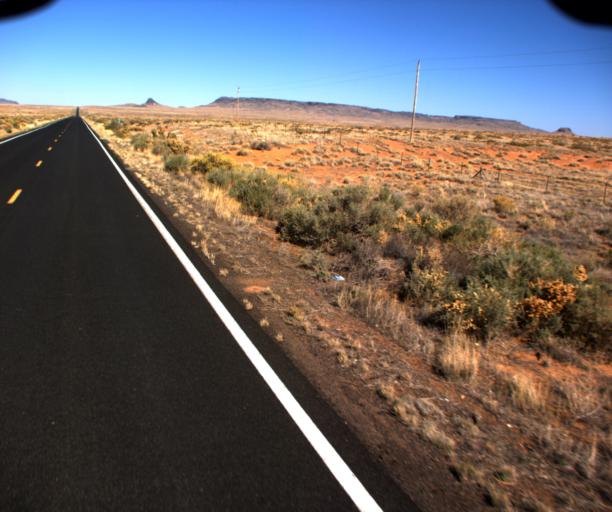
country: US
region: Arizona
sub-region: Navajo County
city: Dilkon
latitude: 35.3436
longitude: -110.4240
